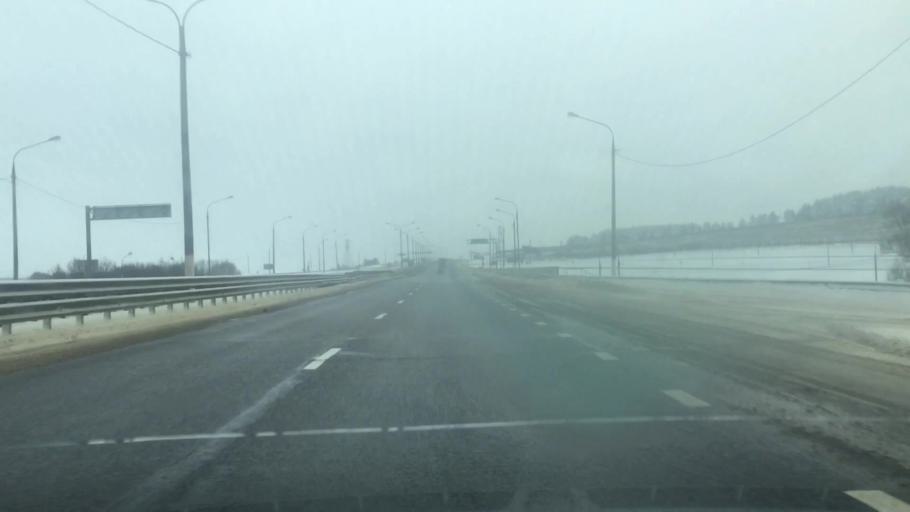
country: RU
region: Tula
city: Yefremov
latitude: 53.1645
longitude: 38.2480
